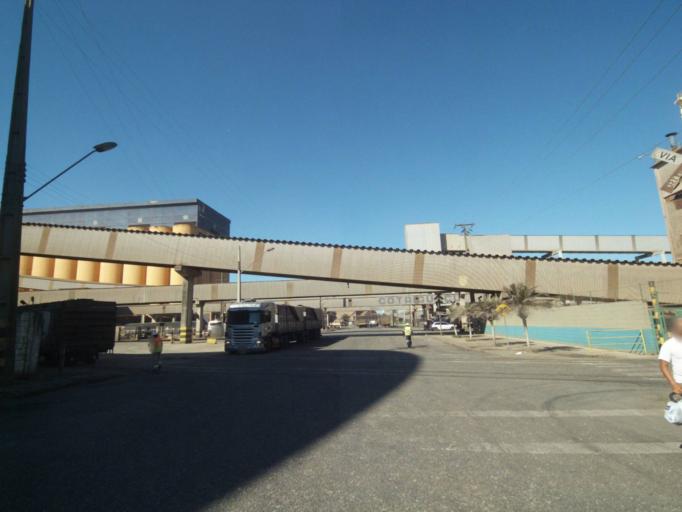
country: BR
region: Parana
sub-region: Paranagua
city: Paranagua
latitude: -25.5041
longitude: -48.5096
